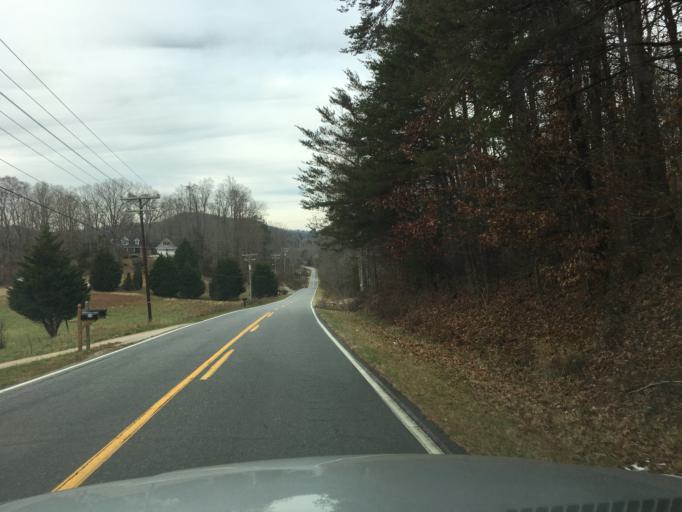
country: US
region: North Carolina
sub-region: McDowell County
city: West Marion
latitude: 35.6230
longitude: -81.9819
